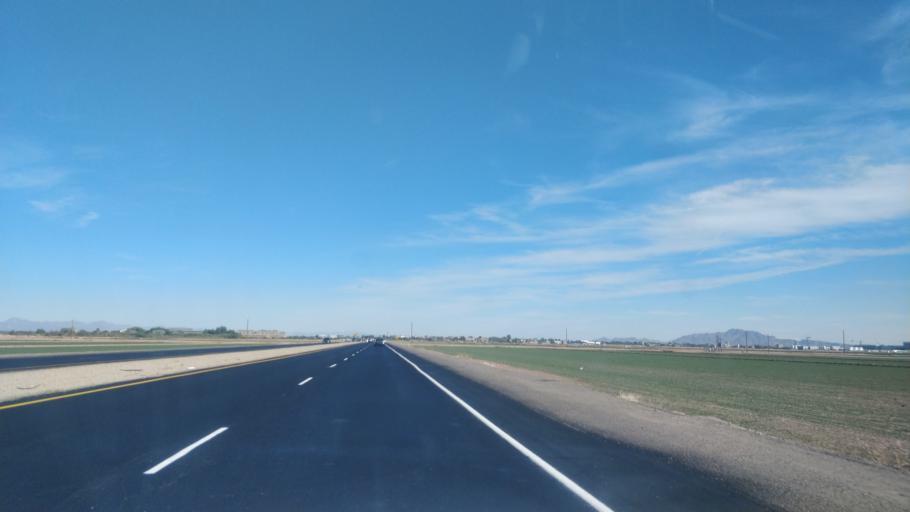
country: US
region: Arizona
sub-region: Maricopa County
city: Sun Lakes
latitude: 33.2609
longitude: -111.9139
